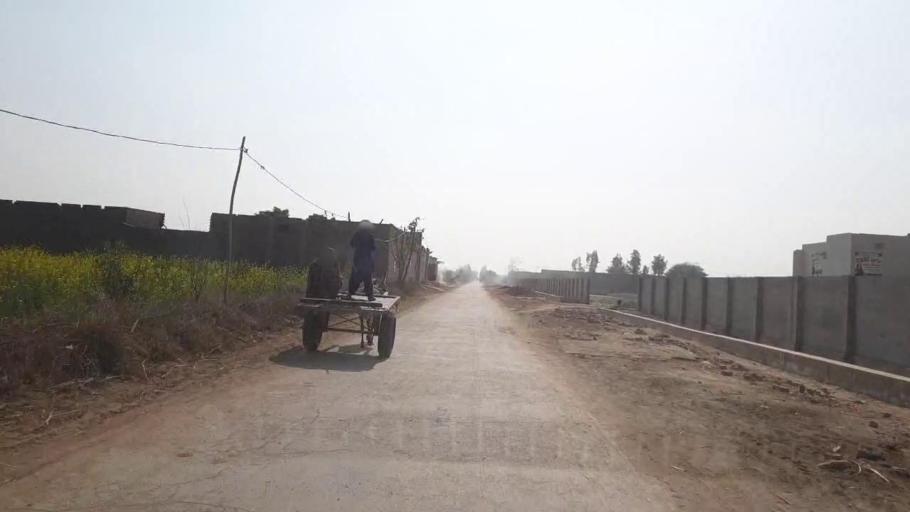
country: PK
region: Sindh
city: Bhit Shah
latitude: 25.7027
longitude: 68.5440
